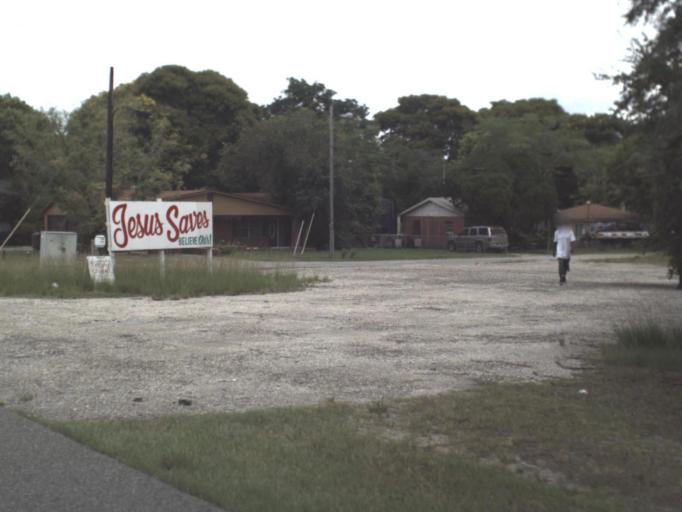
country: US
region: Florida
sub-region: Hillsborough County
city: East Lake-Orient Park
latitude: 27.9815
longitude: -82.3949
